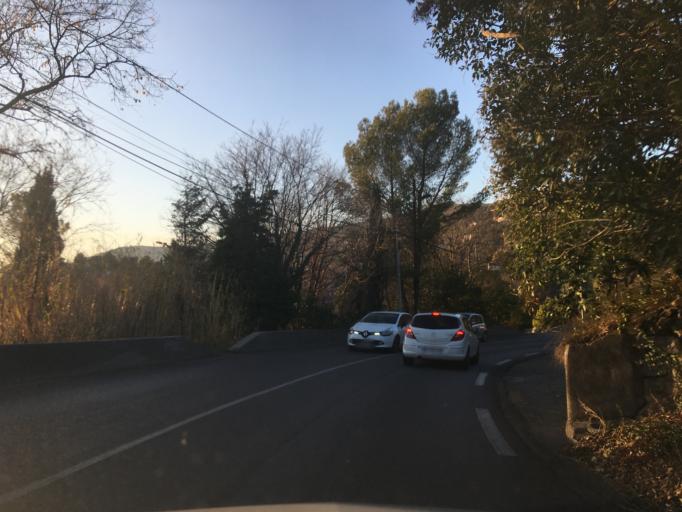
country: FR
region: Provence-Alpes-Cote d'Azur
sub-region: Departement des Alpes-Maritimes
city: Peymeinade
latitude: 43.6432
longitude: 6.9035
